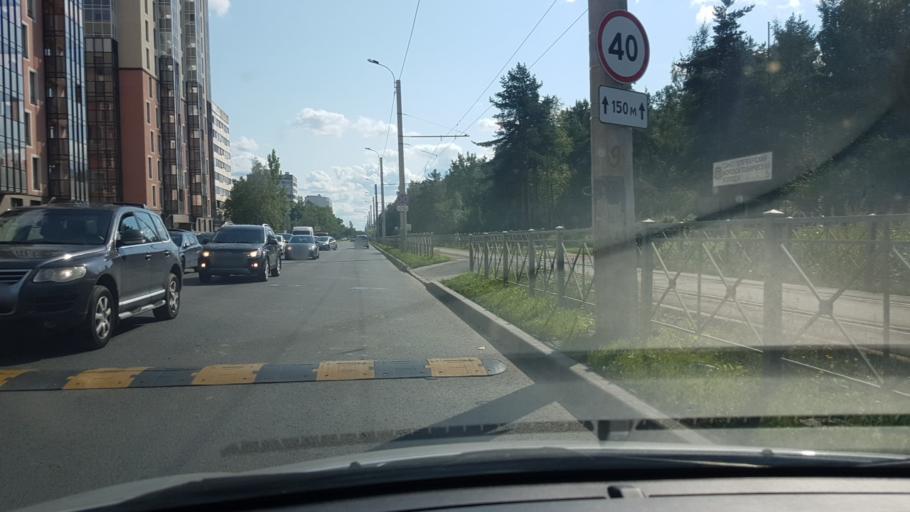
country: RU
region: St.-Petersburg
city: Sosnovaya Polyana
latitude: 59.8323
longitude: 30.1402
